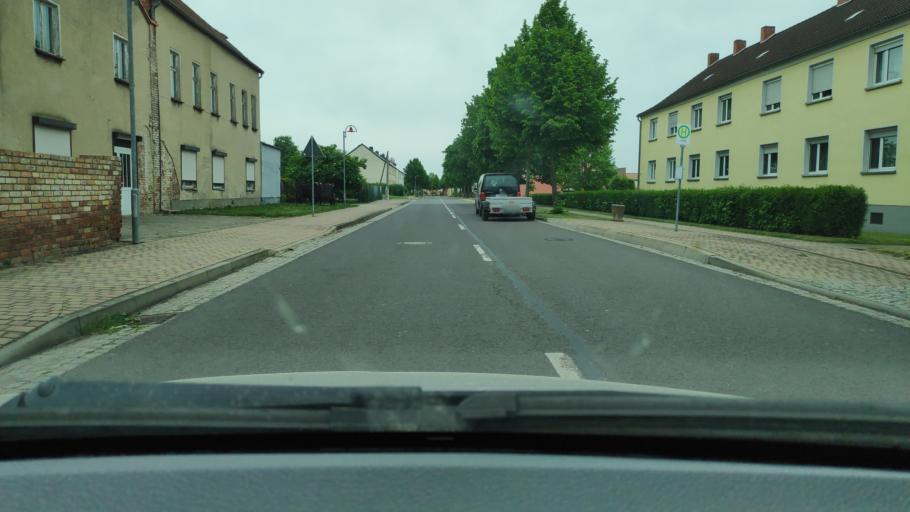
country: DE
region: Saxony-Anhalt
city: Leitzkau
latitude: 51.9926
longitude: 11.9855
